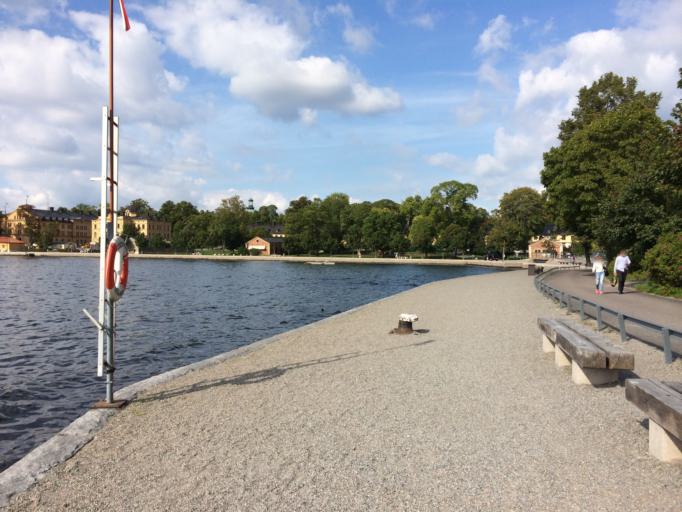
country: SE
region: Stockholm
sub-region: Stockholms Kommun
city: OEstermalm
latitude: 59.3224
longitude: 18.0880
